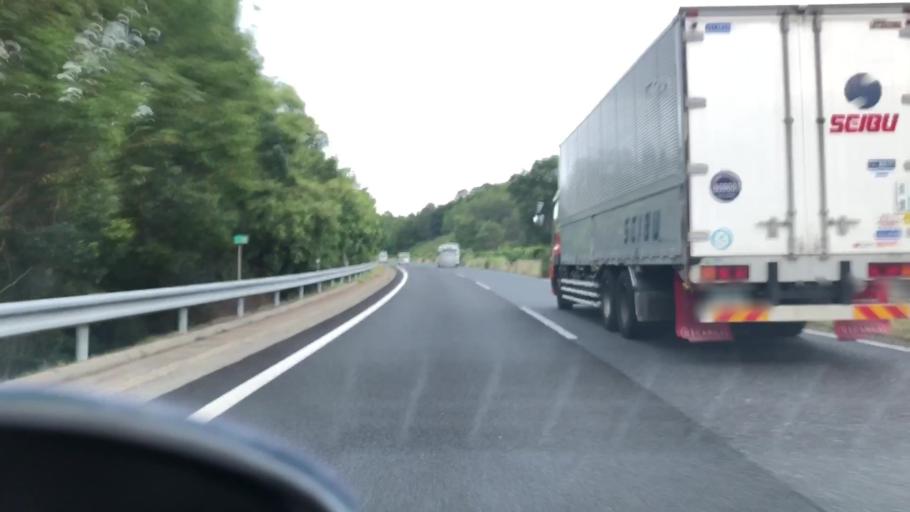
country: JP
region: Hyogo
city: Yashiro
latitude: 34.9154
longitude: 135.0251
